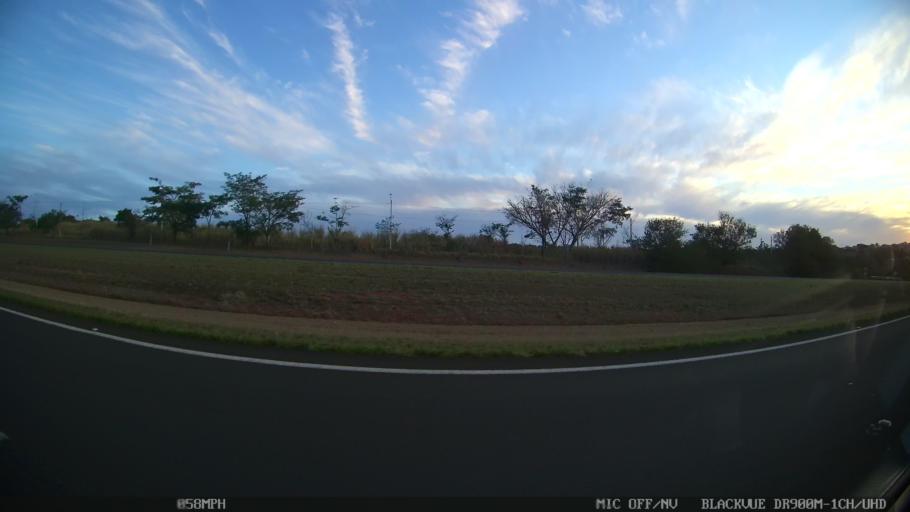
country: BR
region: Sao Paulo
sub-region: Catanduva
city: Catanduva
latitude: -21.1634
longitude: -48.9821
